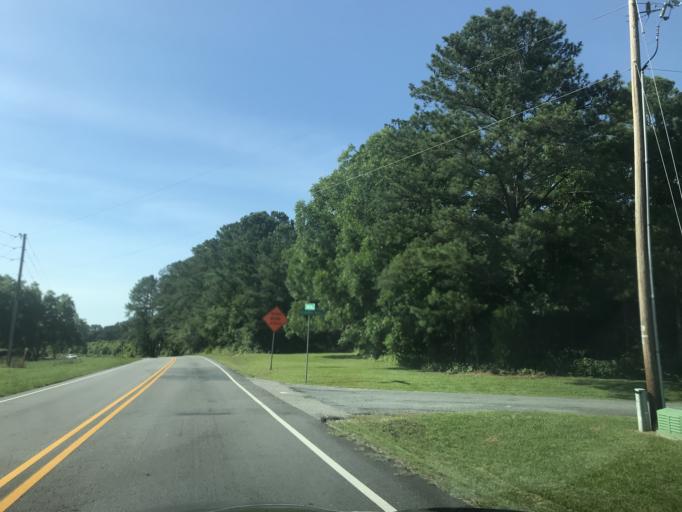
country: US
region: North Carolina
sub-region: Wake County
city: Garner
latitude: 35.6591
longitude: -78.5440
